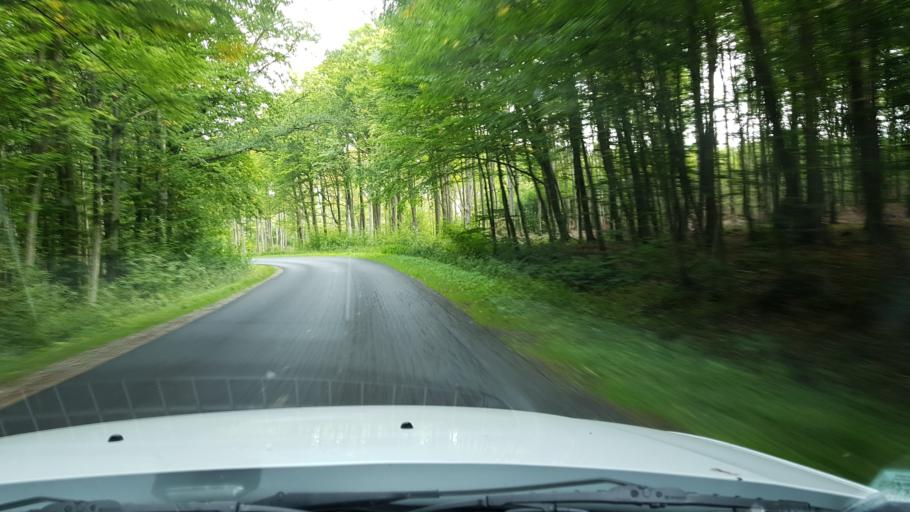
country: PL
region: West Pomeranian Voivodeship
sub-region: Powiat slawienski
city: Slawno
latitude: 54.3945
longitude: 16.6187
